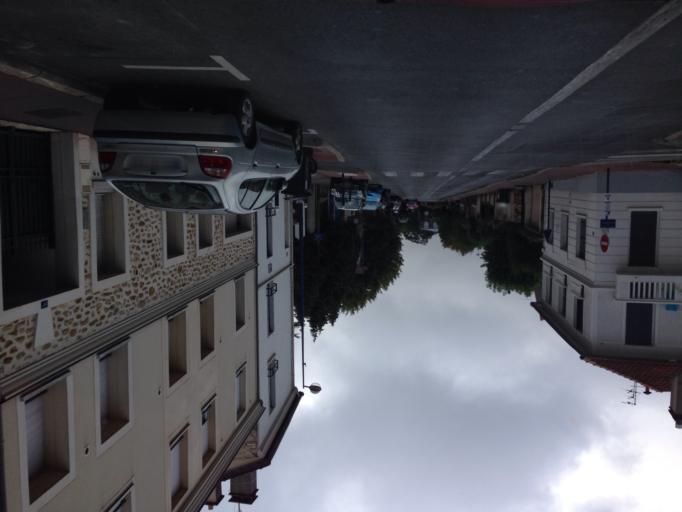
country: FR
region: Ile-de-France
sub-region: Departement des Hauts-de-Seine
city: Clamart
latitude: 48.8042
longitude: 2.2609
